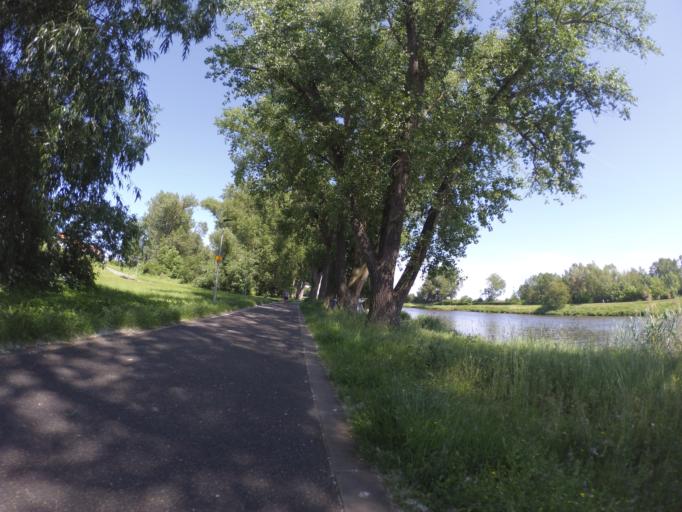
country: CZ
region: Central Bohemia
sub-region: Okres Nymburk
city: Nymburk
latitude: 50.1775
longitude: 15.0256
